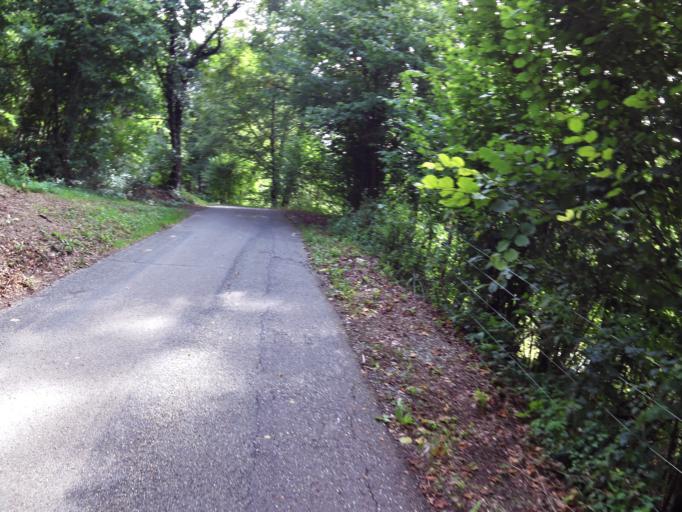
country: DE
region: Baden-Wuerttemberg
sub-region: Freiburg Region
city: Oberndorf
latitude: 48.3268
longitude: 8.5924
